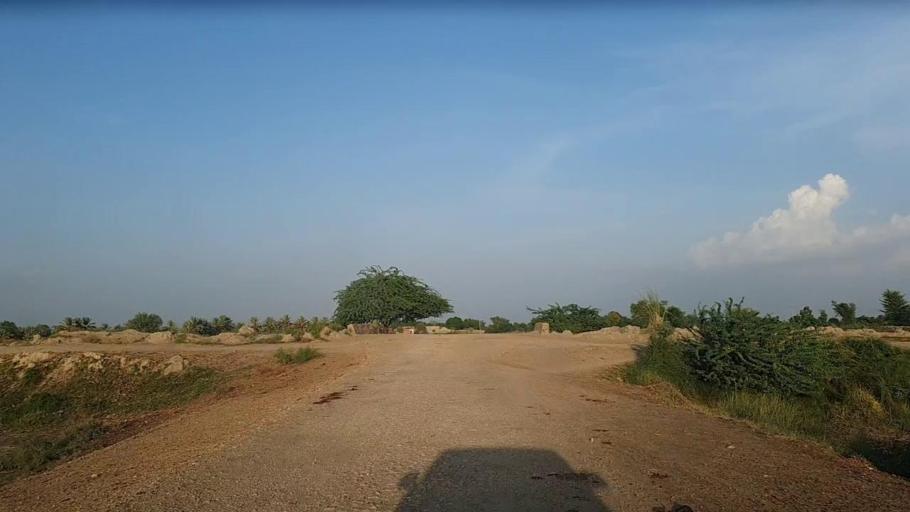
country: PK
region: Sindh
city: Karaundi
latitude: 27.0423
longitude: 68.4125
